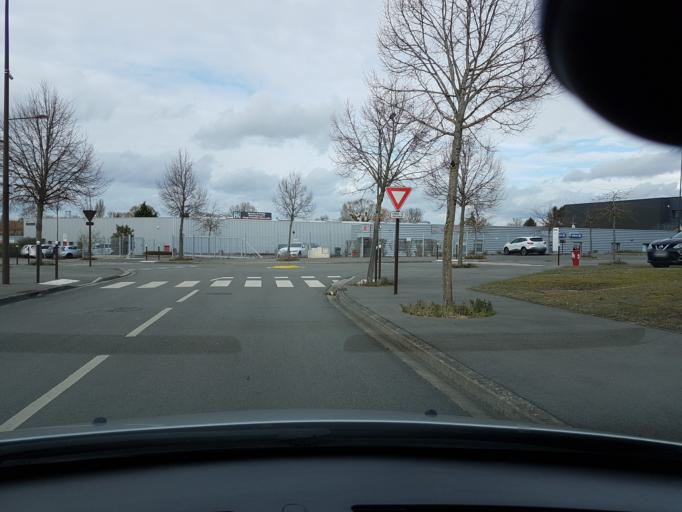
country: FR
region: Centre
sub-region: Departement du Cher
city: Bourges
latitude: 47.0968
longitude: 2.4287
